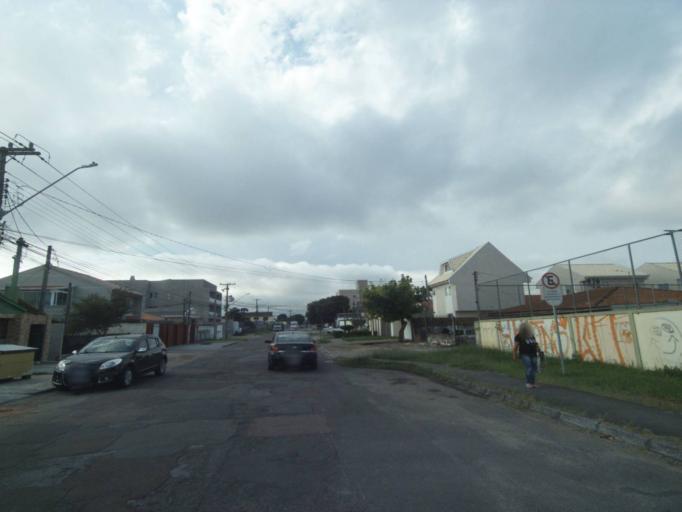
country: BR
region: Parana
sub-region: Pinhais
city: Pinhais
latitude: -25.4581
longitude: -49.2051
